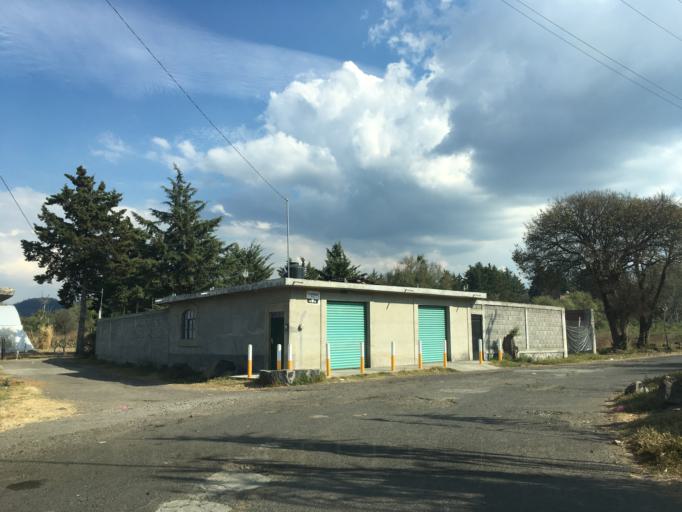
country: MX
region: Michoacan
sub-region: Patzcuaro
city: Santa Ana Chapitiro
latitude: 19.5409
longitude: -101.6397
